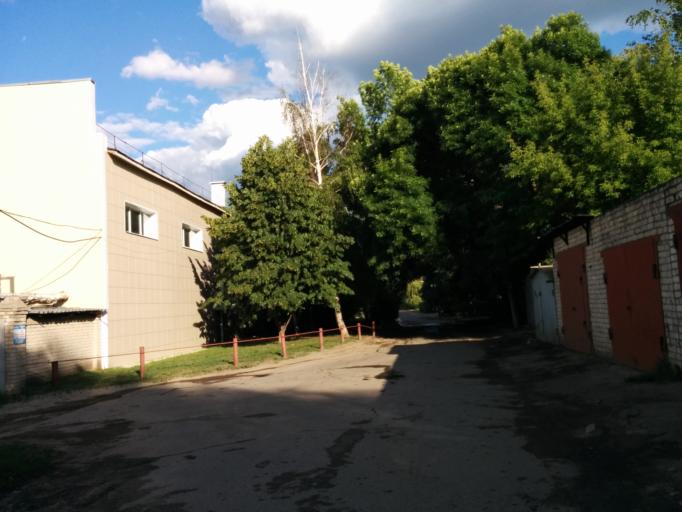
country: RU
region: Tambov
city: Tambov
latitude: 52.7466
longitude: 41.4425
